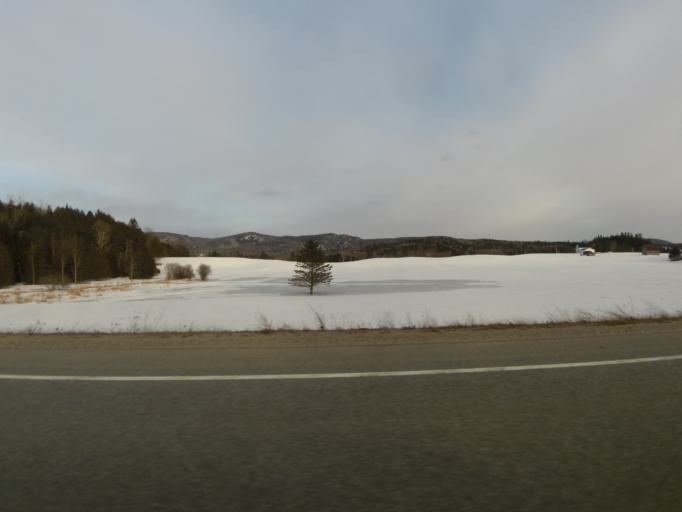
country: CA
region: Quebec
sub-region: Outaouais
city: Wakefield
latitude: 45.7277
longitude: -75.9097
